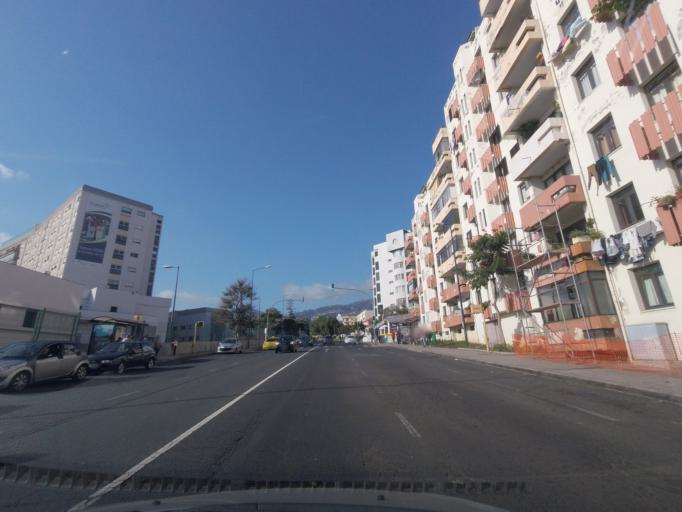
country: PT
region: Madeira
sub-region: Funchal
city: Funchal
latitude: 32.6482
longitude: -16.9233
